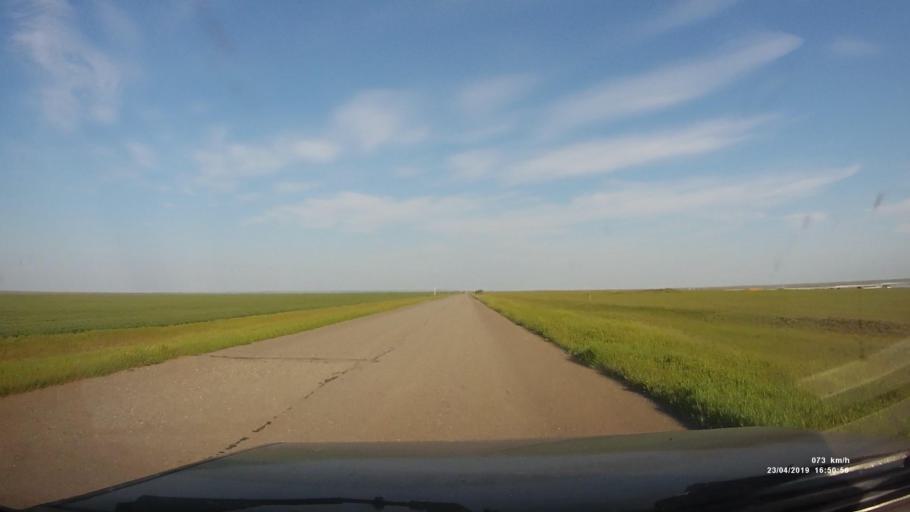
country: RU
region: Kalmykiya
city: Priyutnoye
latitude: 46.3250
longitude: 43.2989
